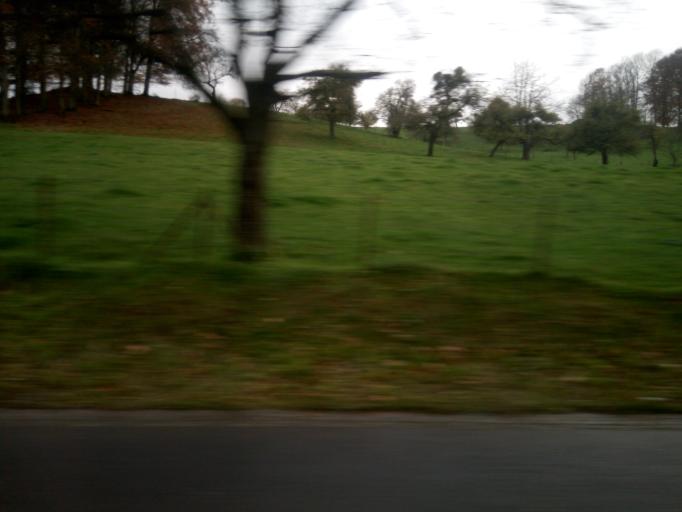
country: LU
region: Diekirch
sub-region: Canton de Vianden
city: Tandel
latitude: 49.8947
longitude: 6.1819
